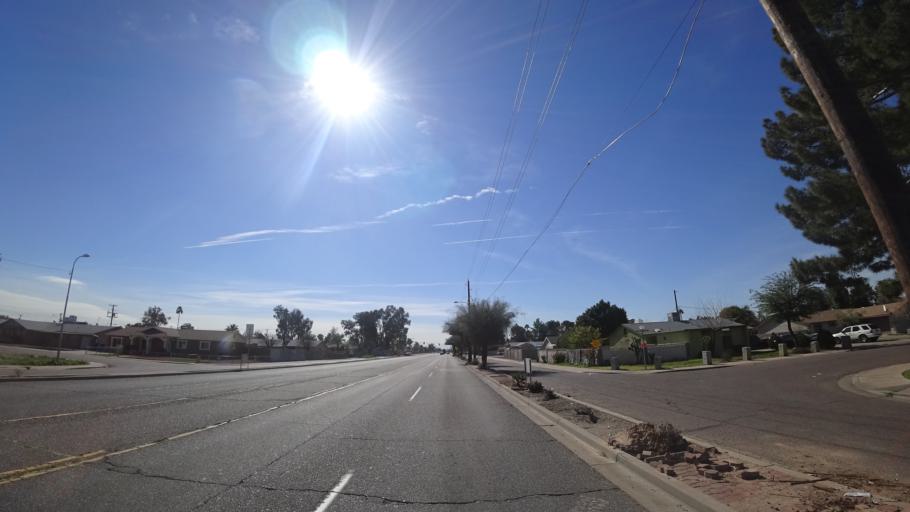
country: US
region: Arizona
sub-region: Maricopa County
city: Glendale
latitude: 33.5041
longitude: -112.1865
